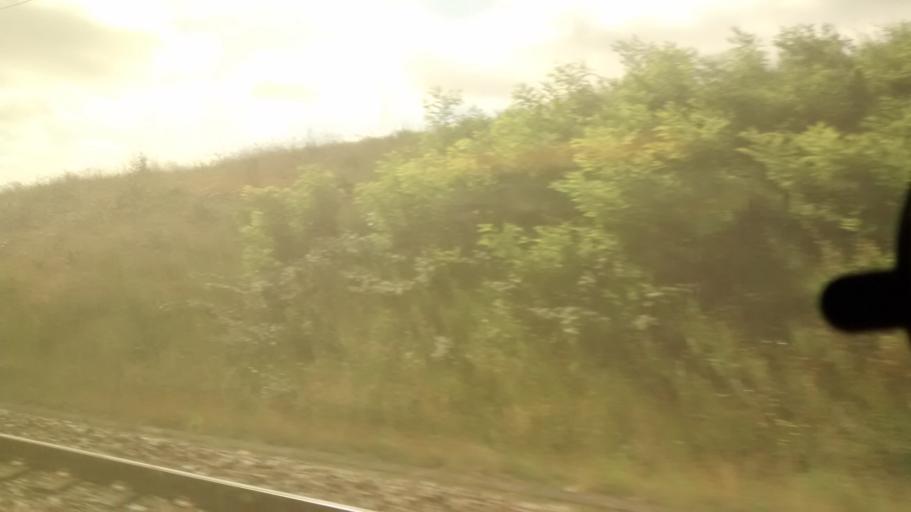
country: FR
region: Pays de la Loire
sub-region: Departement de la Sarthe
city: Vibraye
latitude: 48.0817
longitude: 0.7151
